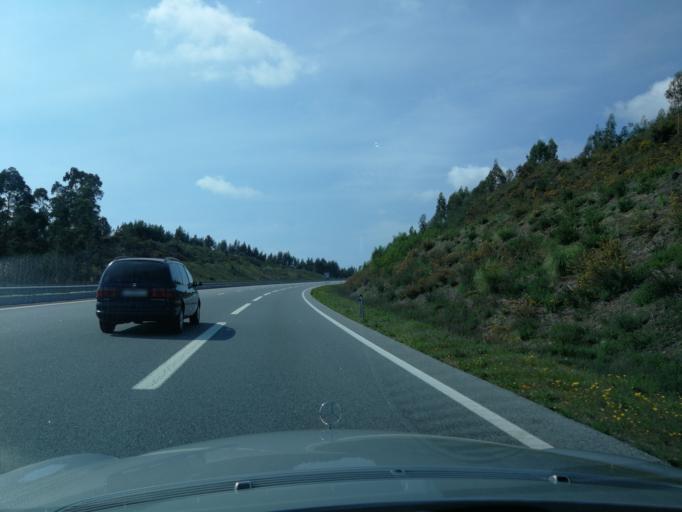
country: PT
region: Braga
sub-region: Vila Nova de Famalicao
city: Ribeirao
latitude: 41.3763
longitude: -8.5627
